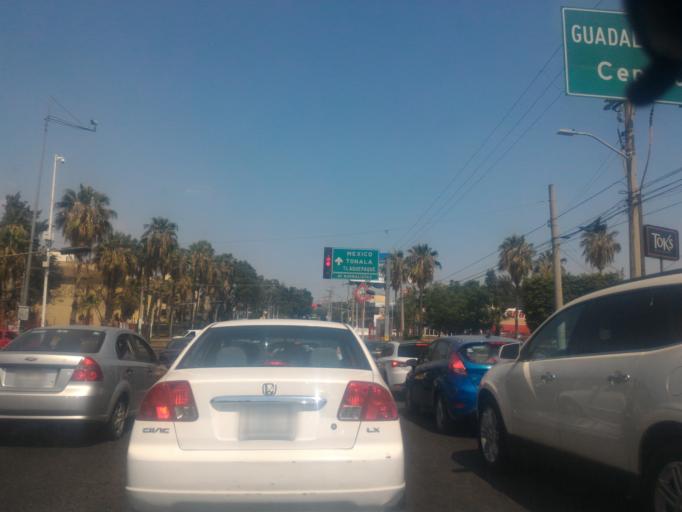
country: MX
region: Jalisco
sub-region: Zapopan
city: Zapopan
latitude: 20.7001
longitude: -103.3364
